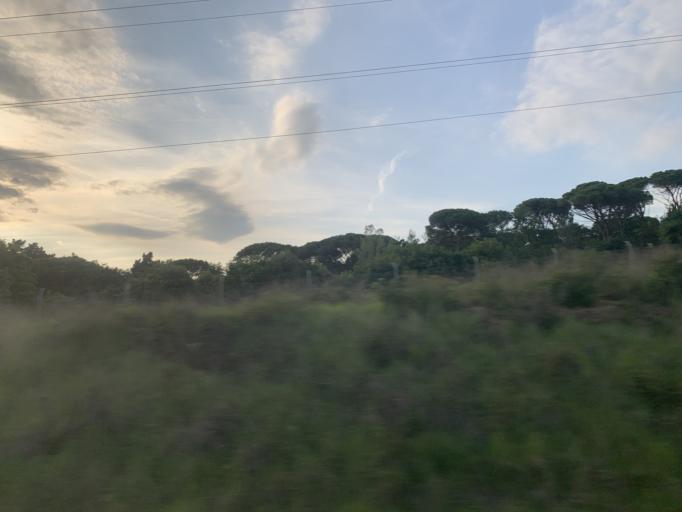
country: ES
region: Catalonia
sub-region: Provincia de Girona
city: Hostalric
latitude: 41.7453
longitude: 2.6205
